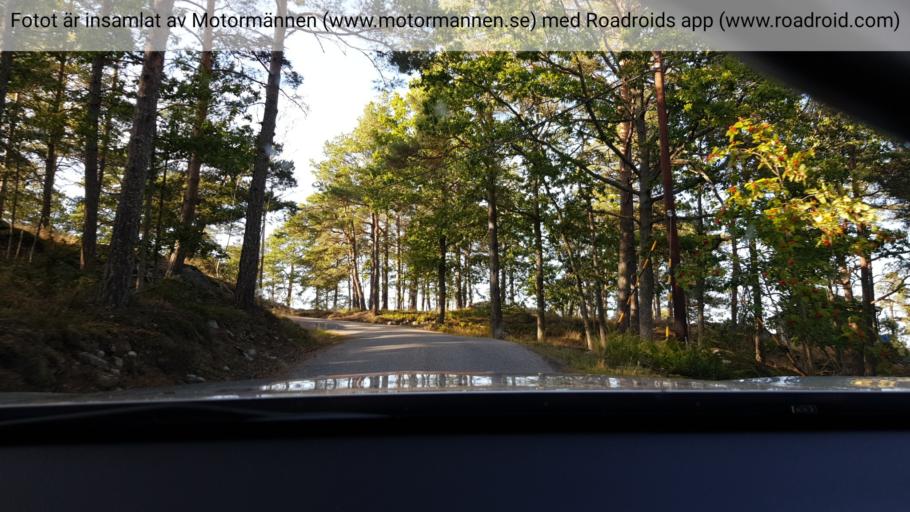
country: SE
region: Stockholm
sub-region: Haninge Kommun
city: Jordbro
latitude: 59.0202
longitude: 18.1001
